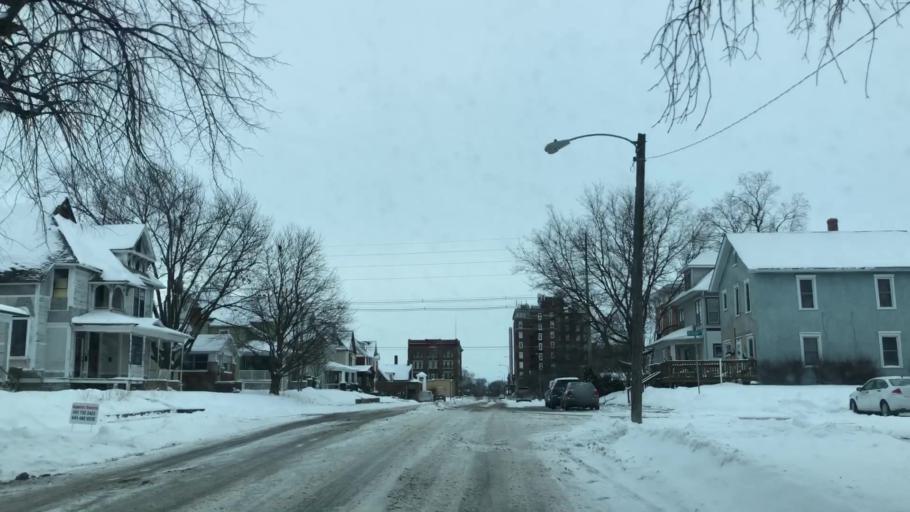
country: US
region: Iowa
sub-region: Marshall County
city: Marshalltown
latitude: 42.0519
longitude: -92.9097
